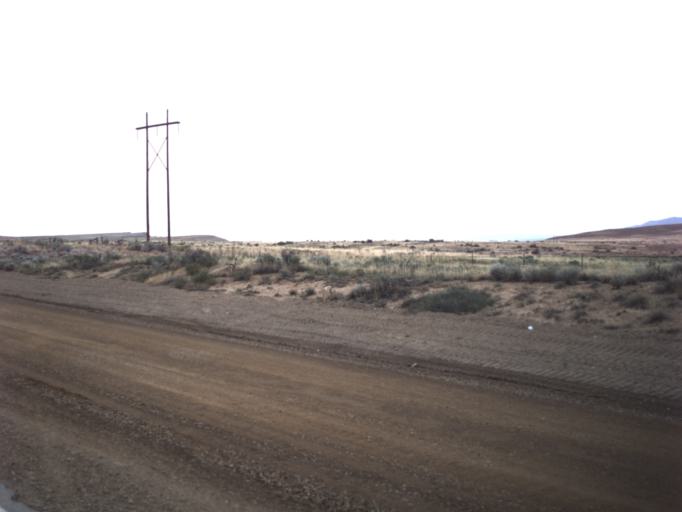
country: US
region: Utah
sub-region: Carbon County
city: East Carbon City
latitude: 39.4470
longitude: -110.4711
